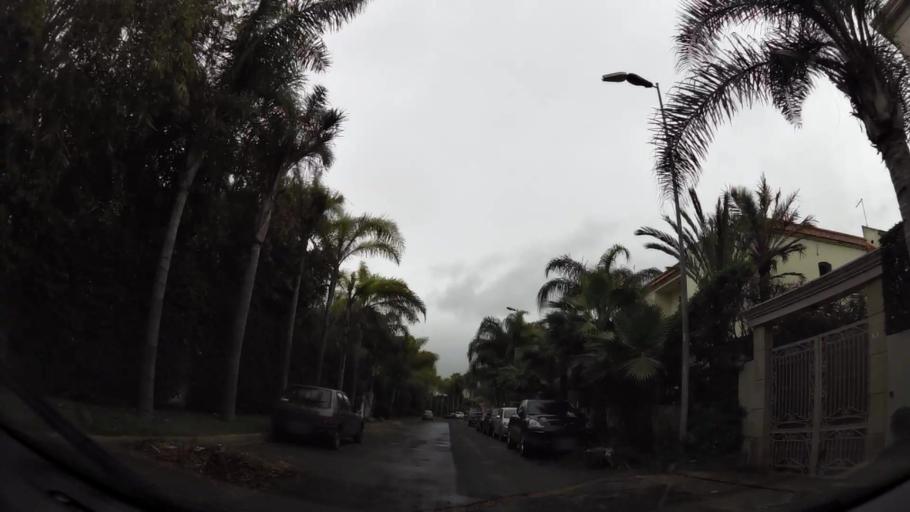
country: MA
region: Grand Casablanca
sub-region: Casablanca
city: Casablanca
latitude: 33.5397
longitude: -7.6292
